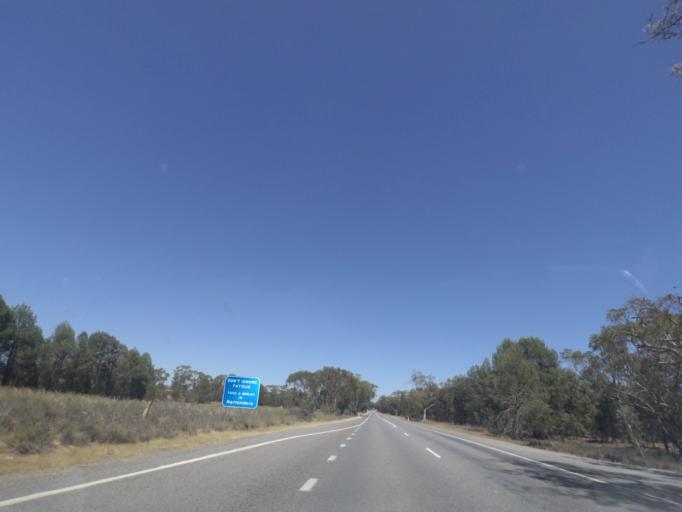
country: AU
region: New South Wales
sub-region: Narrandera
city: Narrandera
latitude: -34.7380
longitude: 146.5808
